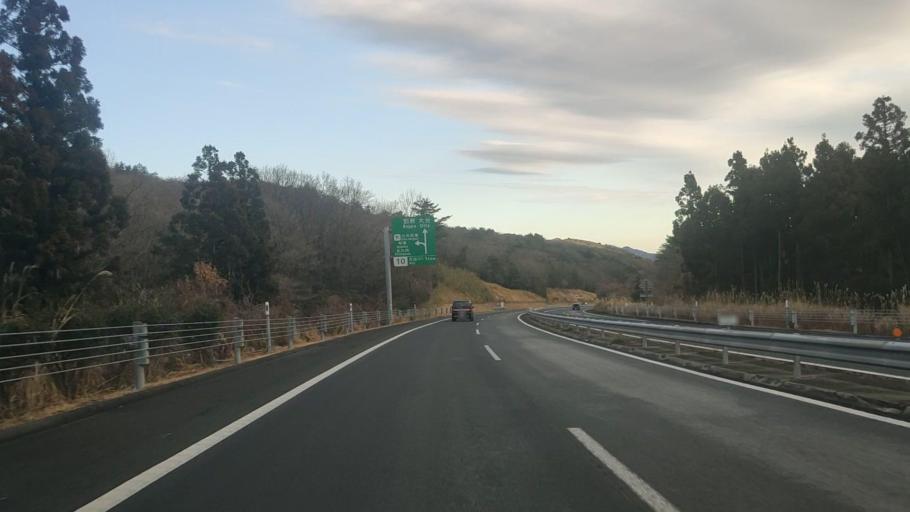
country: JP
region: Oita
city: Beppu
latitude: 33.3458
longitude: 131.4282
